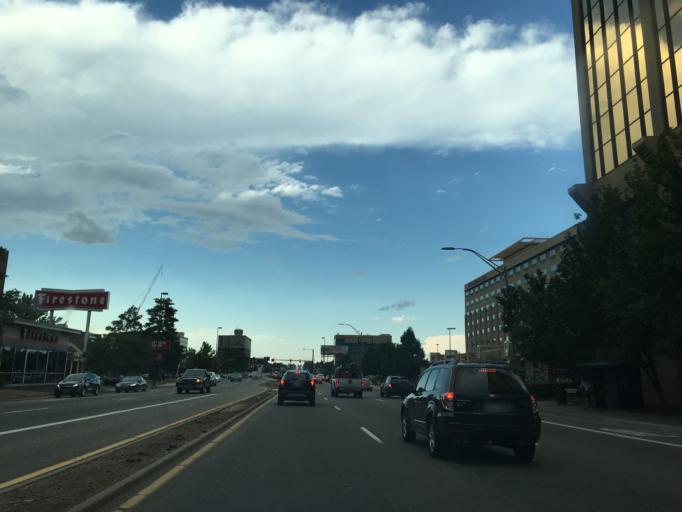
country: US
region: Colorado
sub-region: Arapahoe County
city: Glendale
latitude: 39.7041
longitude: -104.9406
